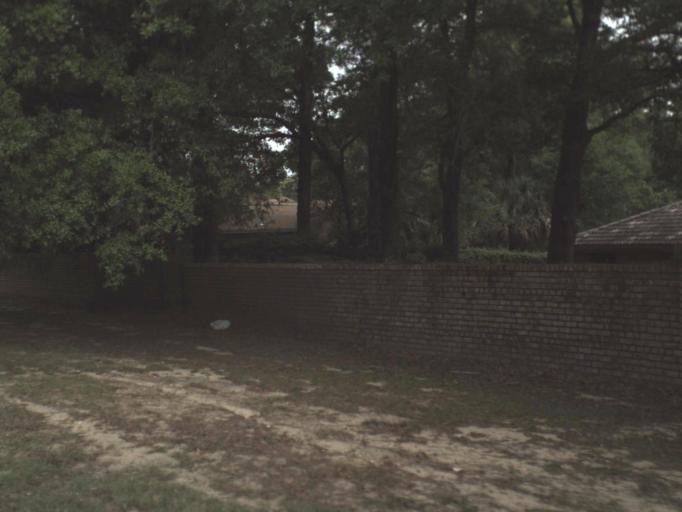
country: US
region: Florida
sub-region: Escambia County
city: East Pensacola Heights
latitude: 30.4416
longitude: -87.1820
